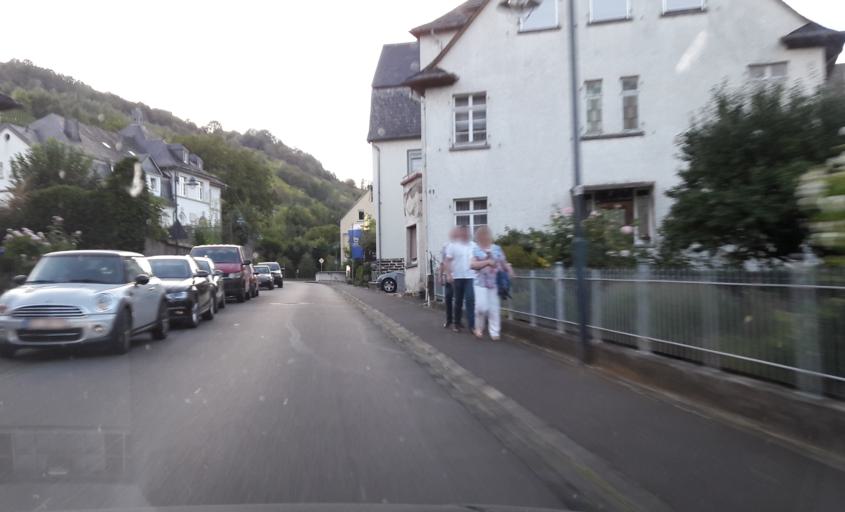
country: DE
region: Rheinland-Pfalz
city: Reil
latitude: 50.0232
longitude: 7.1151
